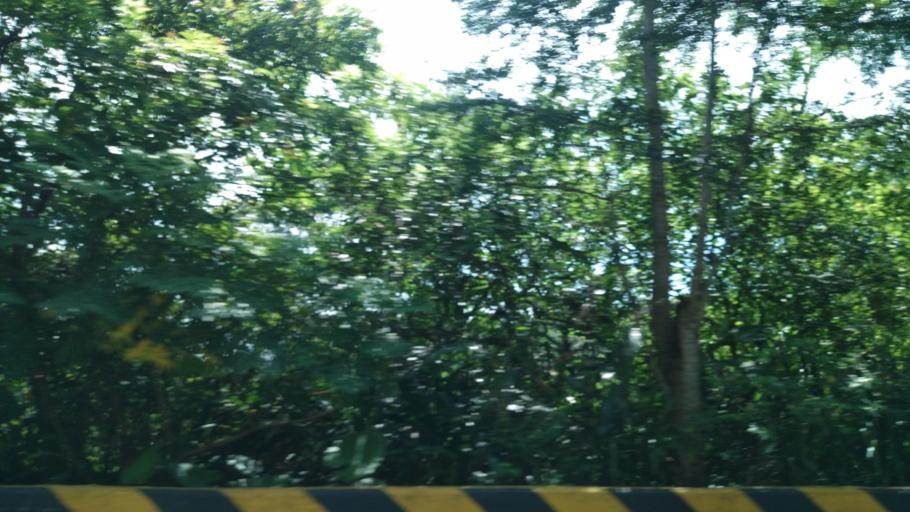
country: TW
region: Taipei
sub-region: Taipei
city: Banqiao
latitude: 24.9449
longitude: 121.5043
